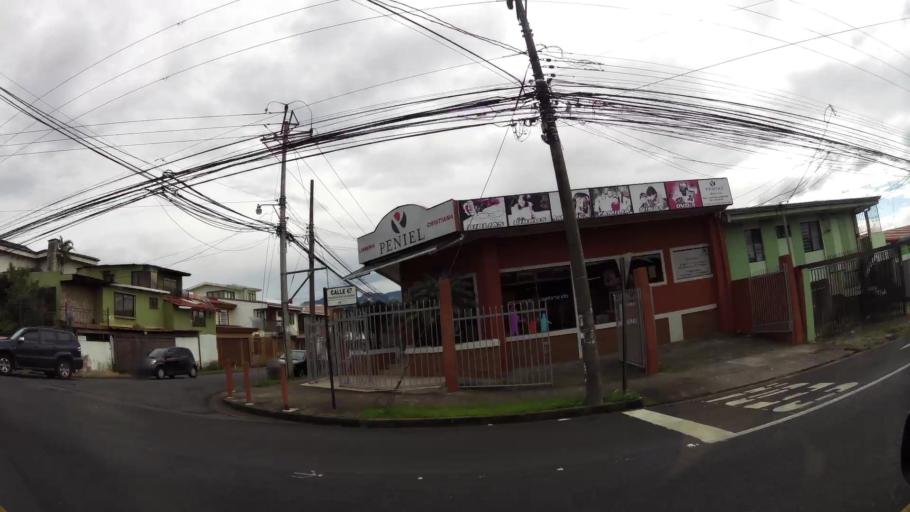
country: CR
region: San Jose
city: San Vicente
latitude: 9.9562
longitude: -84.0482
